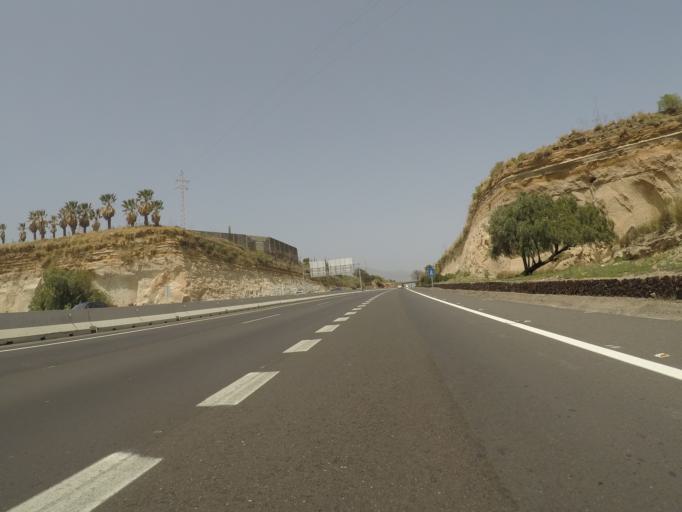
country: ES
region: Canary Islands
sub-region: Provincia de Santa Cruz de Tenerife
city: Guimar
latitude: 28.3061
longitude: -16.3832
